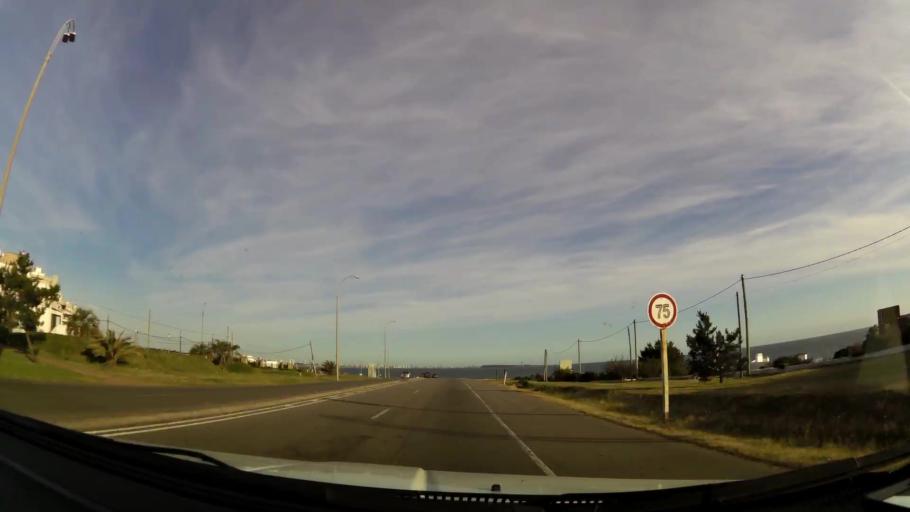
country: UY
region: Maldonado
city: Maldonado
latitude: -34.9081
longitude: -55.0195
